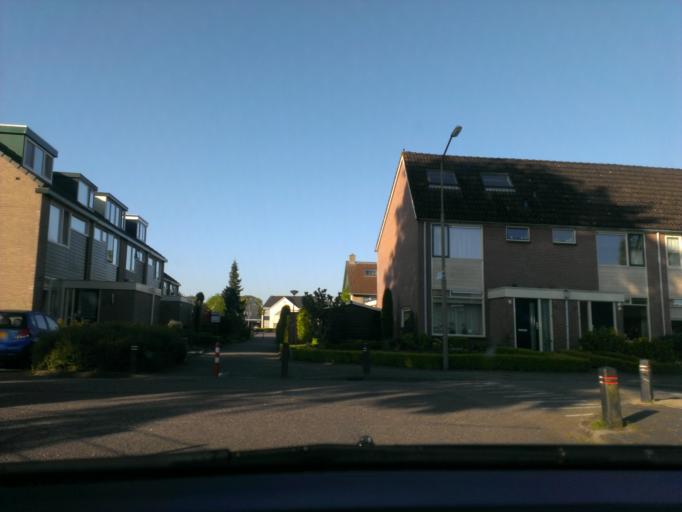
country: NL
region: Gelderland
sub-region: Gemeente Heerde
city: Heerde
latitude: 52.3821
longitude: 6.0397
